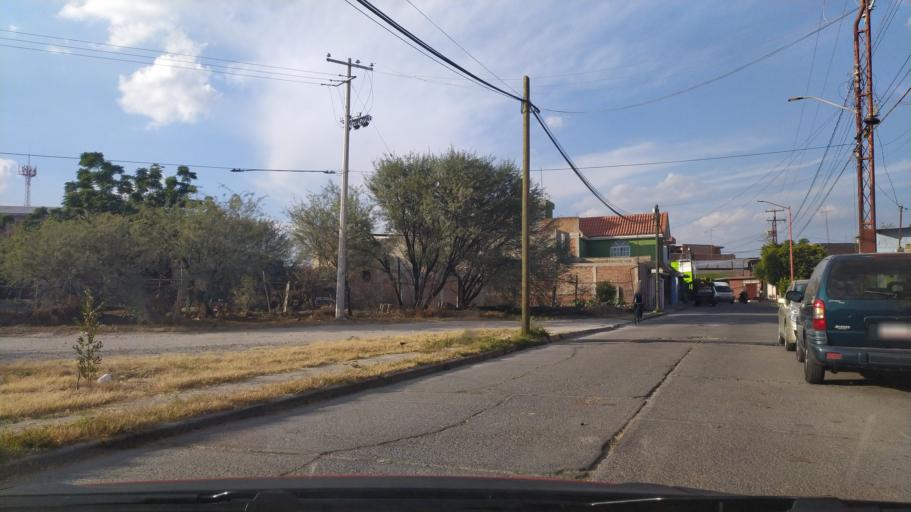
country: MX
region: Guanajuato
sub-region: Purisima del Rincon
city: Monte Grande
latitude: 21.0090
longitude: -101.8673
